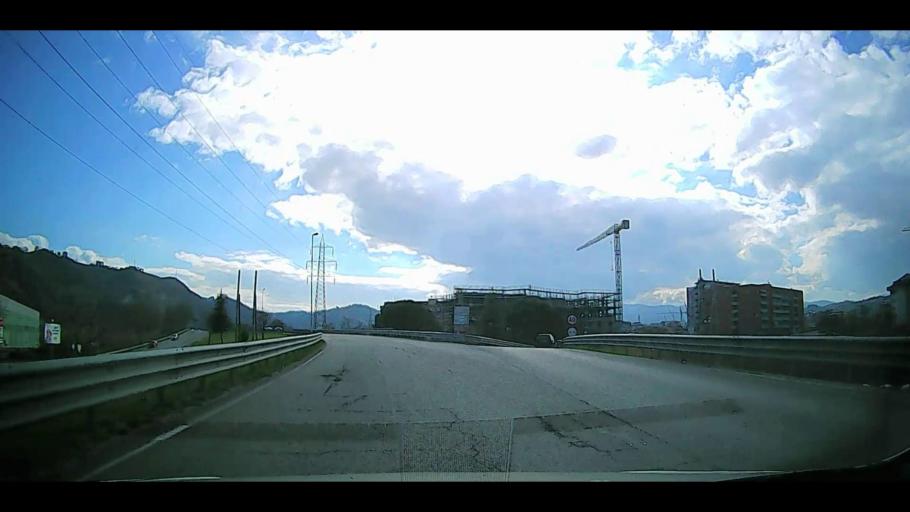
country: IT
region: Calabria
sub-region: Provincia di Cosenza
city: Cosenza
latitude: 39.3147
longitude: 16.2583
